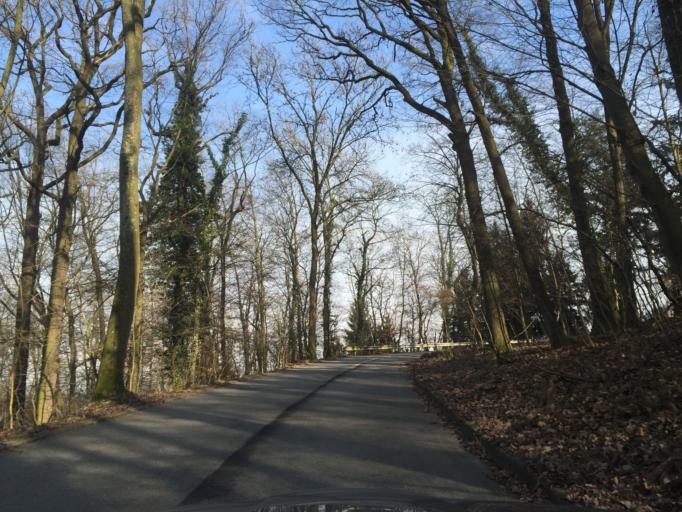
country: DE
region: Baden-Wuerttemberg
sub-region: Karlsruhe Region
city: Weinheim
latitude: 49.5521
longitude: 8.6825
